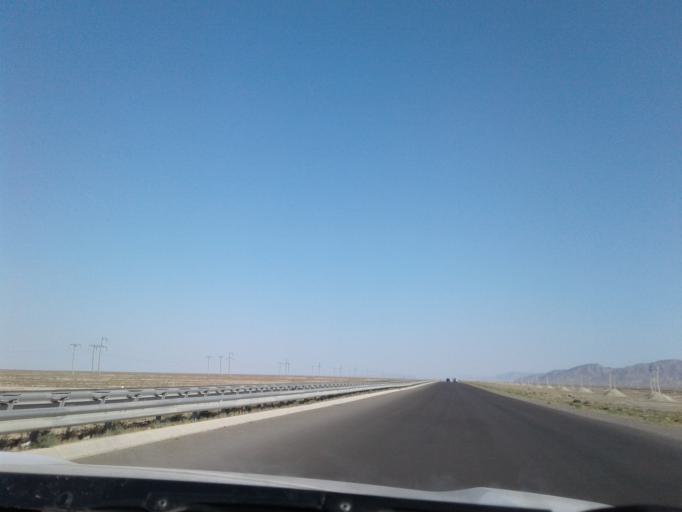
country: TM
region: Balkan
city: Serdar
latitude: 39.1239
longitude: 55.9013
